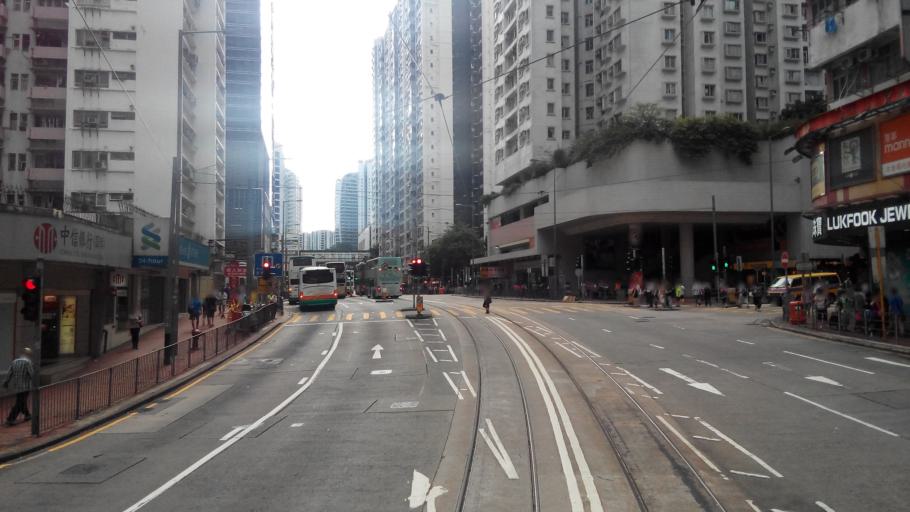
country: HK
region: Wanchai
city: Wan Chai
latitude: 22.2847
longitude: 114.2126
